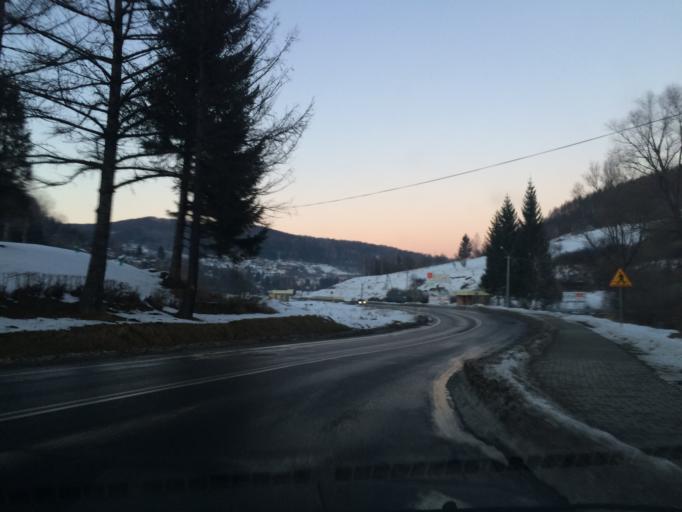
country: PL
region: Subcarpathian Voivodeship
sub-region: Powiat bieszczadzki
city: Ustrzyki Dolne
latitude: 49.4225
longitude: 22.5758
